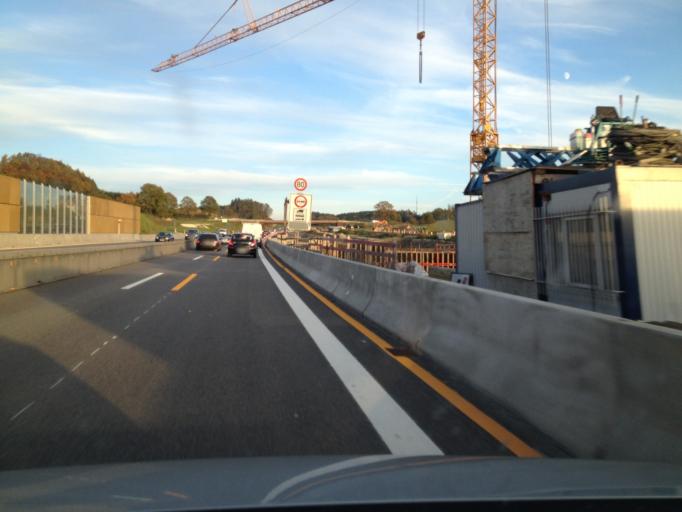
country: DE
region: Bavaria
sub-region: Swabia
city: Zusmarshausen
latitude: 48.4099
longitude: 10.5932
